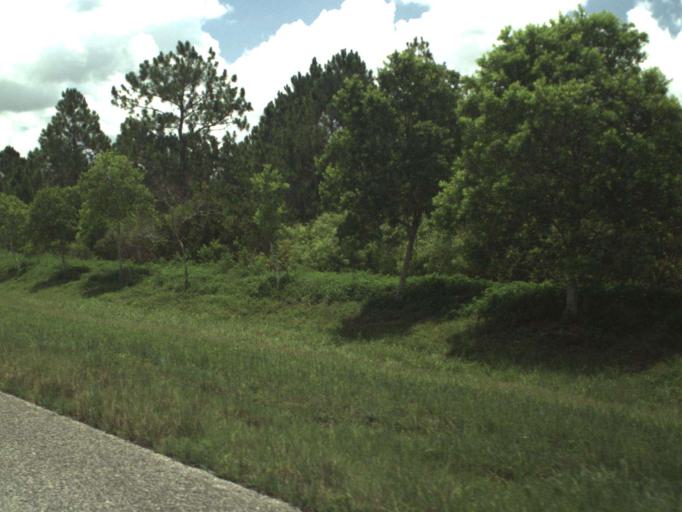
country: US
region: Florida
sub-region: Indian River County
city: Fellsmere
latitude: 27.6814
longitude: -80.8581
